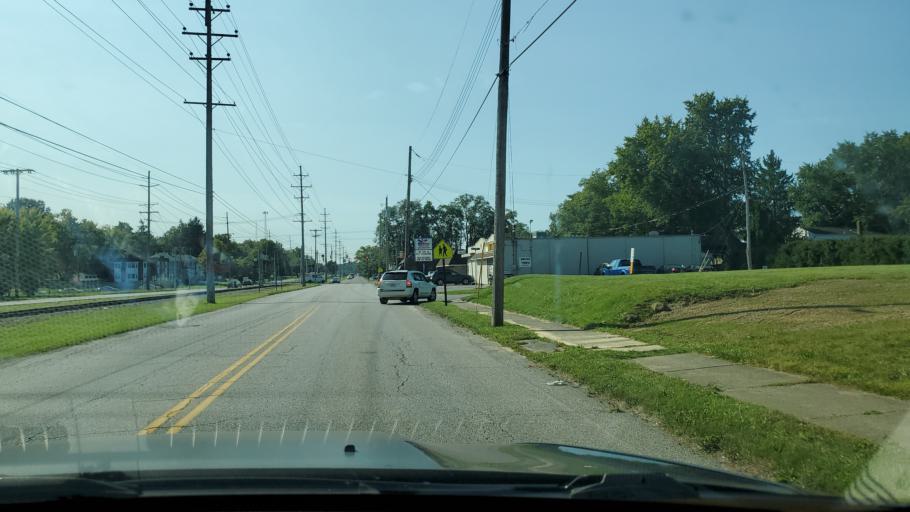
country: US
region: Ohio
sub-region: Mahoning County
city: Boardman
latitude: 41.0480
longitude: -80.6579
